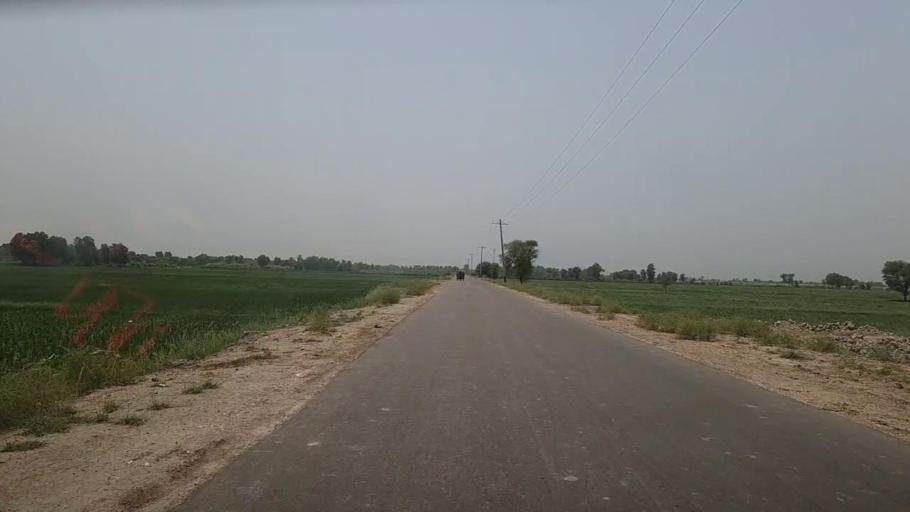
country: PK
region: Sindh
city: Sita Road
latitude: 27.0506
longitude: 67.9019
